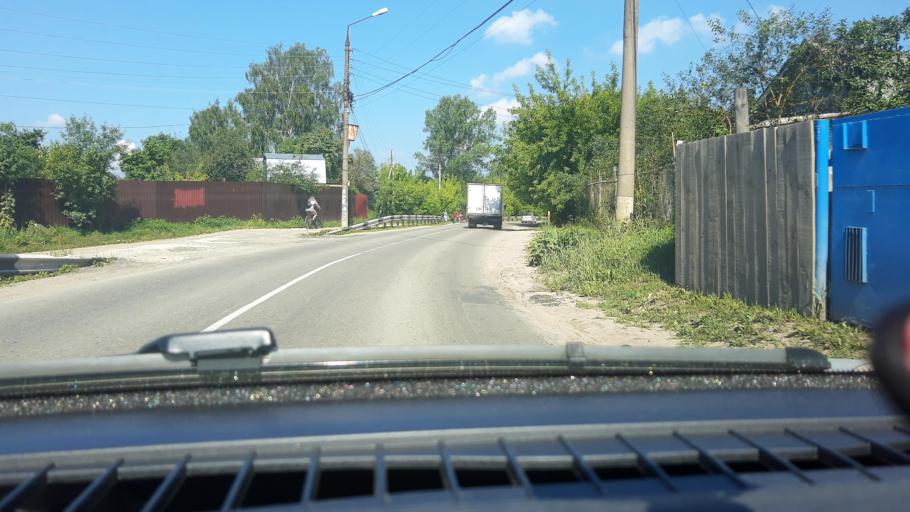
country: RU
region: Nizjnij Novgorod
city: Afonino
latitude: 56.2937
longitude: 44.1895
